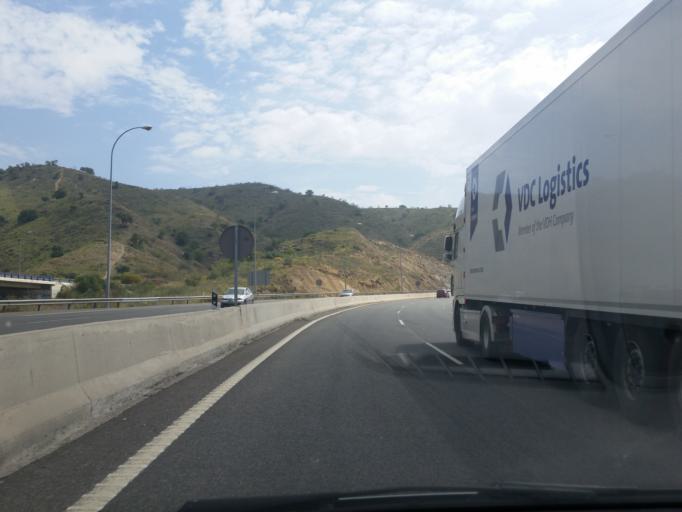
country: ES
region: Andalusia
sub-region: Provincia de Malaga
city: Malaga
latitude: 36.7565
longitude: -4.4193
